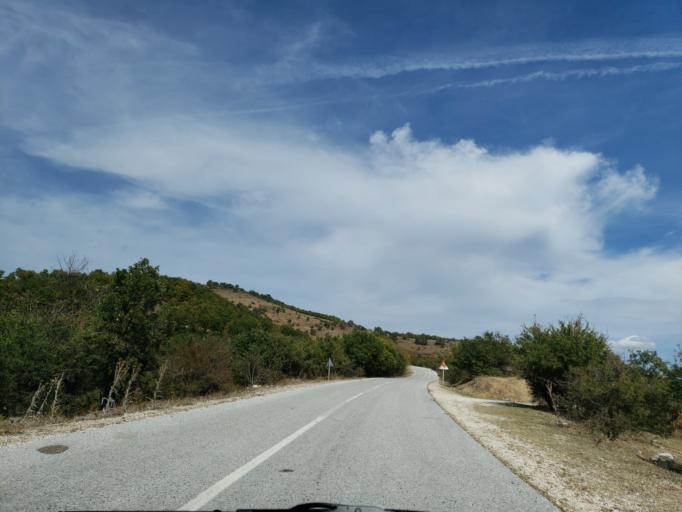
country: GR
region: Thessaly
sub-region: Trikala
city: Kastraki
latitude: 39.7461
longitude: 21.6596
